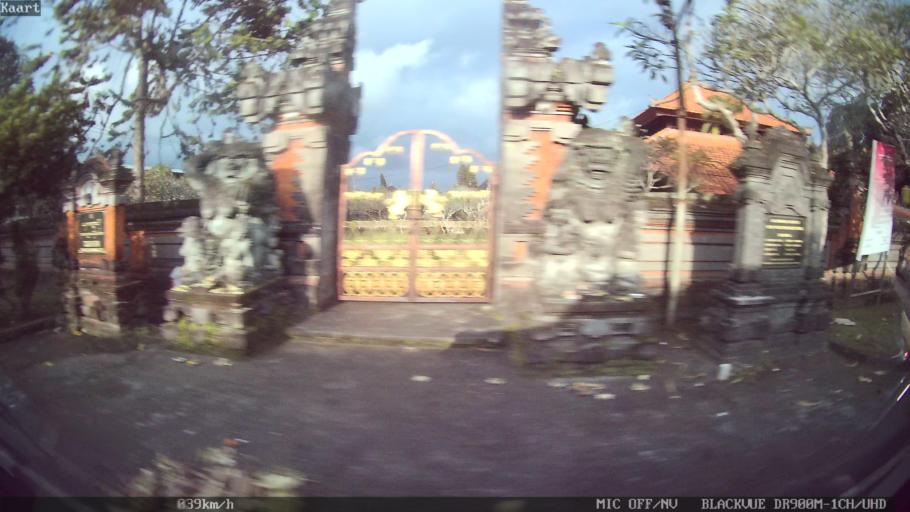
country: ID
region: Bali
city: Banjar Tebongkang
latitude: -8.5311
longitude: 115.2511
